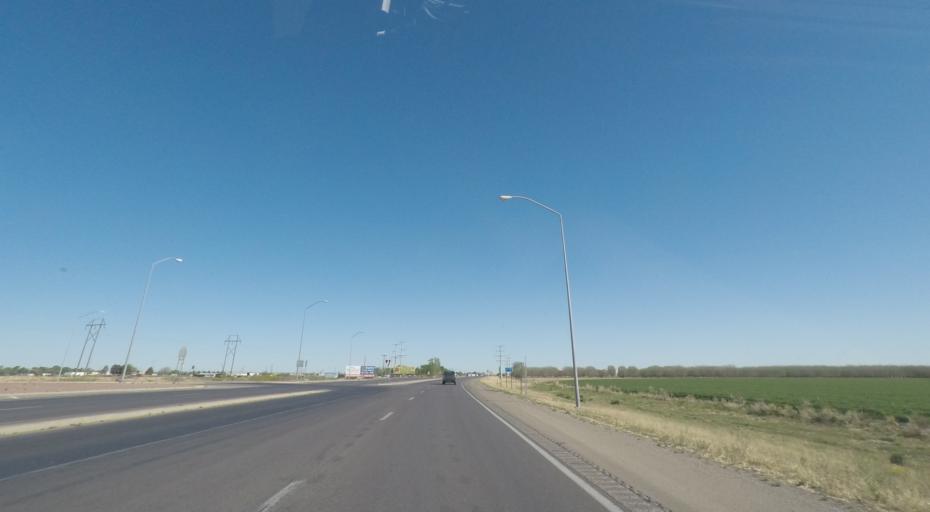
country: US
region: New Mexico
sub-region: Chaves County
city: Roswell
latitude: 33.3307
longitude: -104.5044
